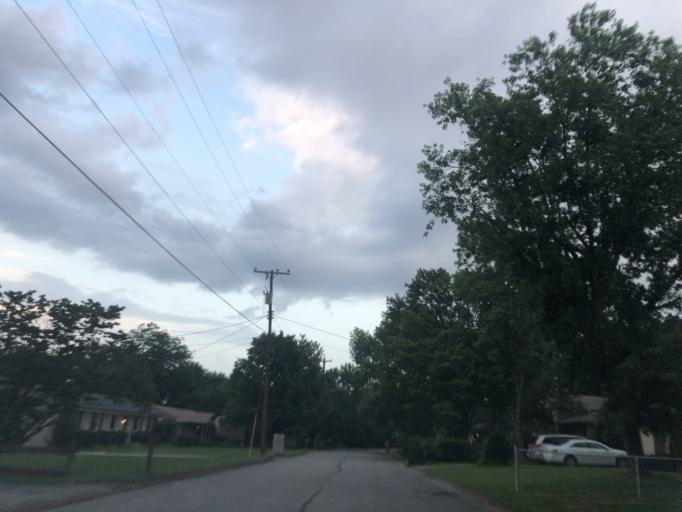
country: US
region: Tennessee
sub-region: Davidson County
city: Lakewood
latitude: 36.1526
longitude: -86.6327
